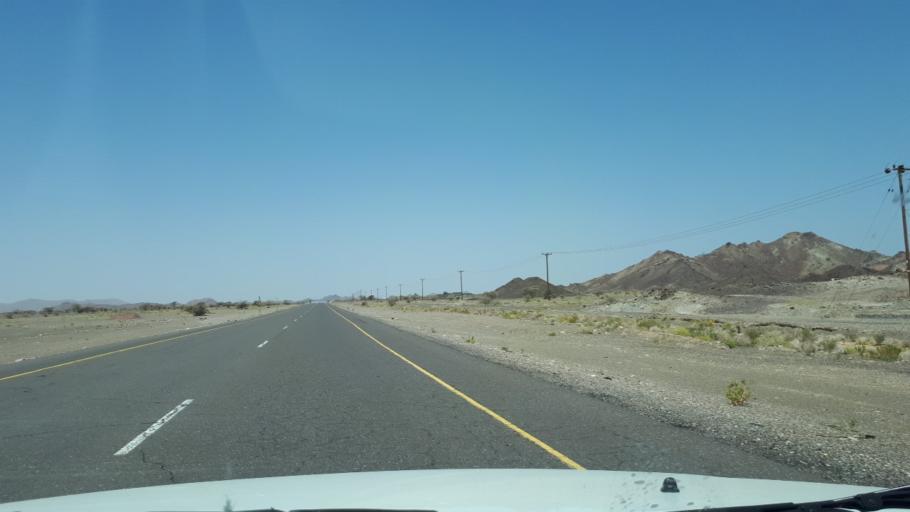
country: OM
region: Ash Sharqiyah
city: Ibra'
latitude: 22.6182
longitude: 58.4369
